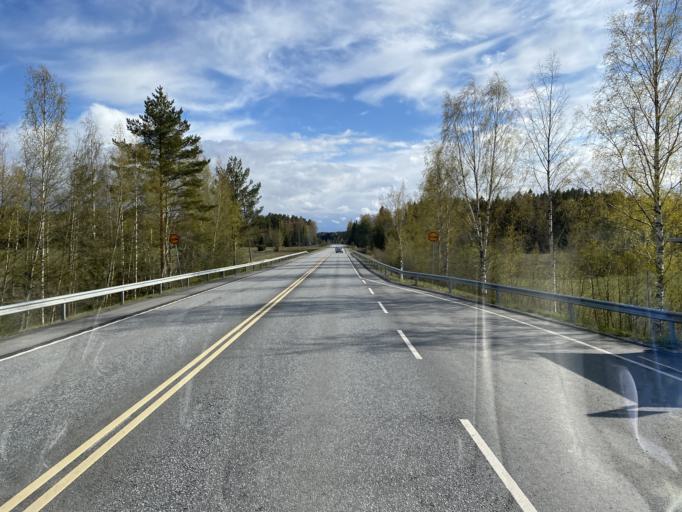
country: FI
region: Pirkanmaa
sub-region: Tampere
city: Lempaeaelae
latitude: 61.2666
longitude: 23.7454
